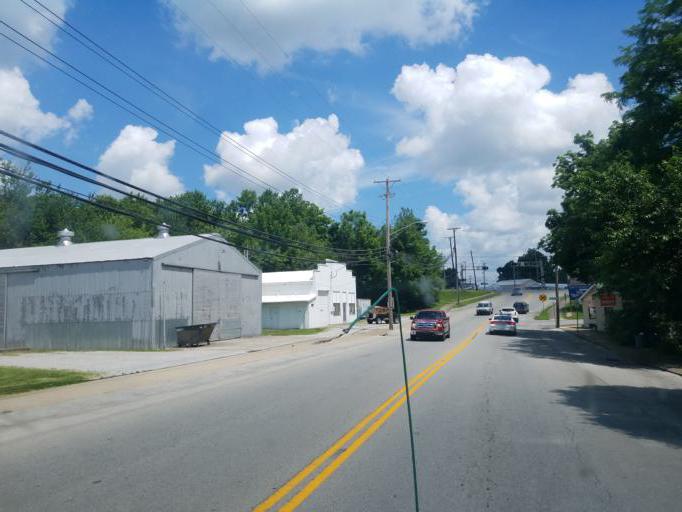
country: US
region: Kentucky
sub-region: Grayson County
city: Leitchfield
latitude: 37.4860
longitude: -86.2929
